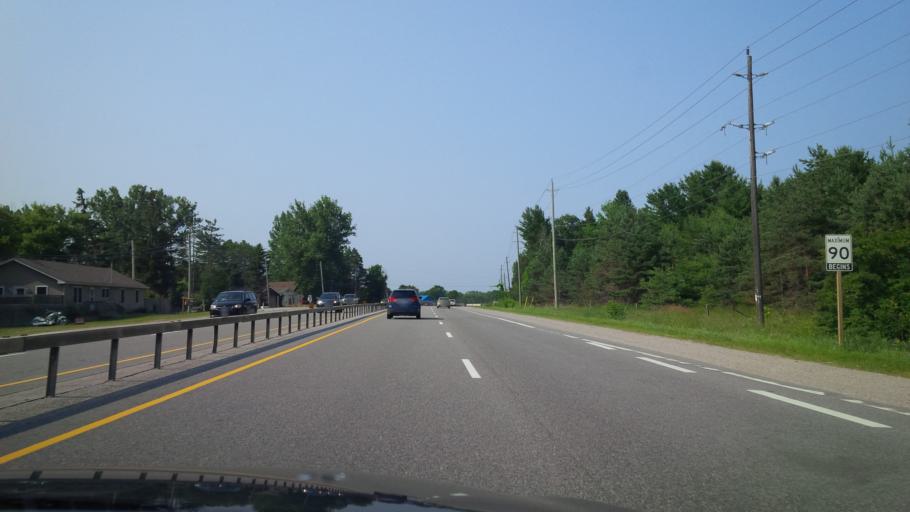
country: CA
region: Ontario
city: Orillia
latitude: 44.7091
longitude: -79.3860
